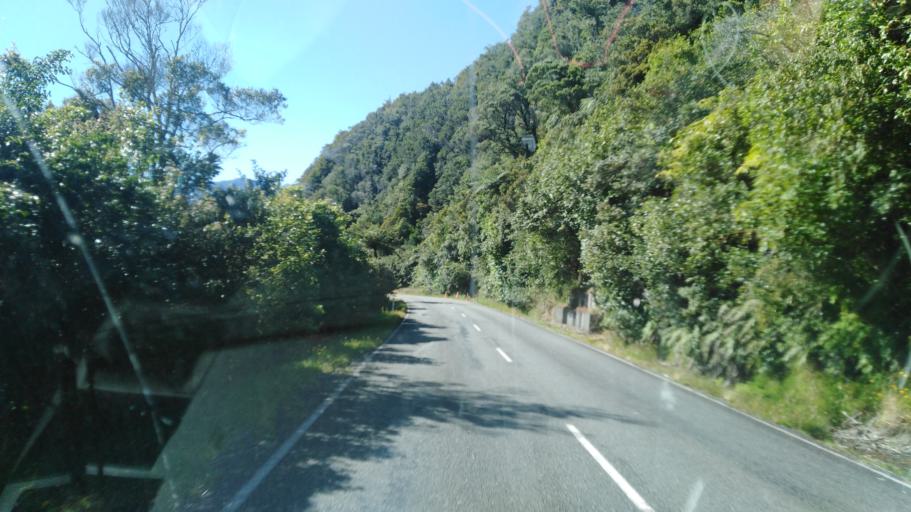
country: NZ
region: West Coast
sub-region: Buller District
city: Westport
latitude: -41.5327
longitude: 171.9547
